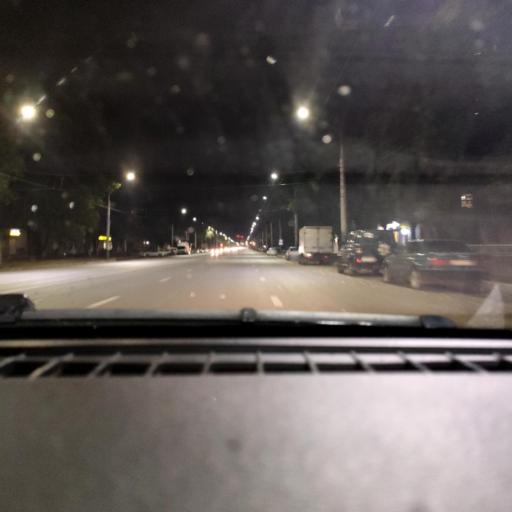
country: RU
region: Voronezj
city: Voronezh
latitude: 51.6429
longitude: 39.2373
